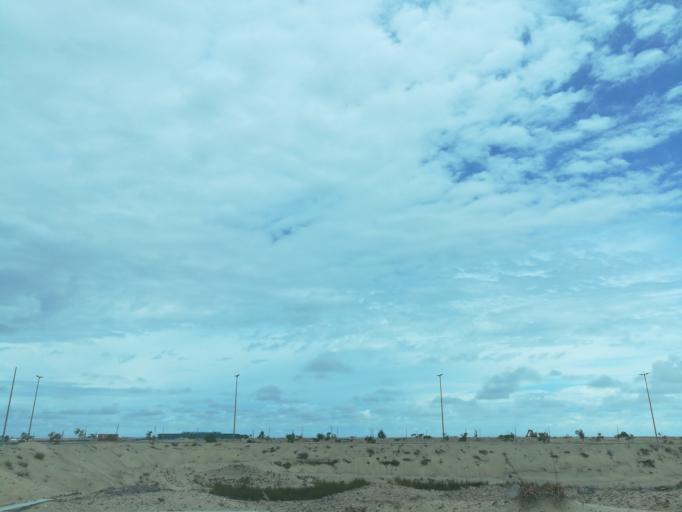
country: NG
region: Lagos
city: Ikoyi
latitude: 6.4120
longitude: 3.4219
